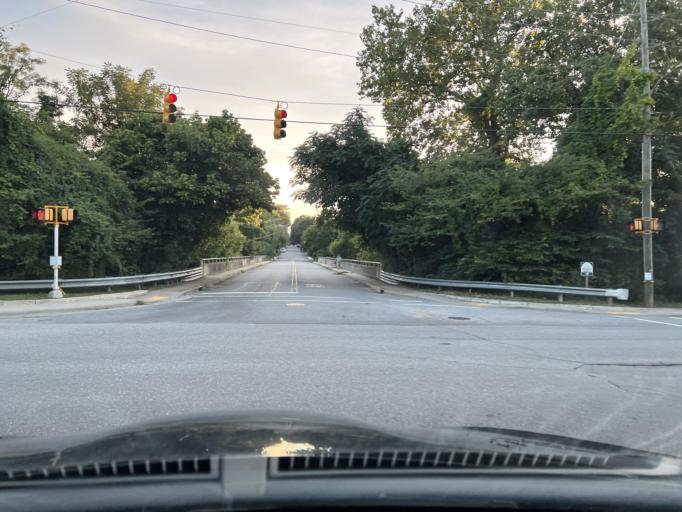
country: US
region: North Carolina
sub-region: Buncombe County
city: Asheville
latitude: 35.6035
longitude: -82.5574
